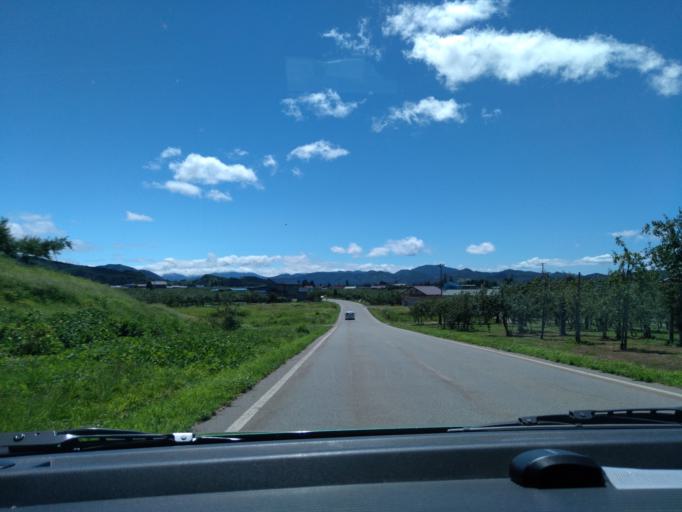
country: JP
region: Akita
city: Yuzawa
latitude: 39.2172
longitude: 140.5665
